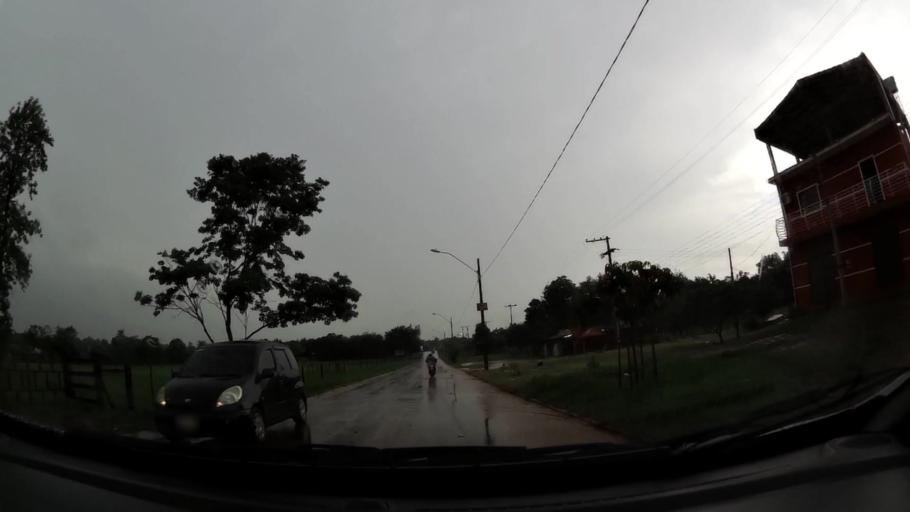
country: PY
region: Alto Parana
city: Presidente Franco
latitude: -25.5262
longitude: -54.6779
